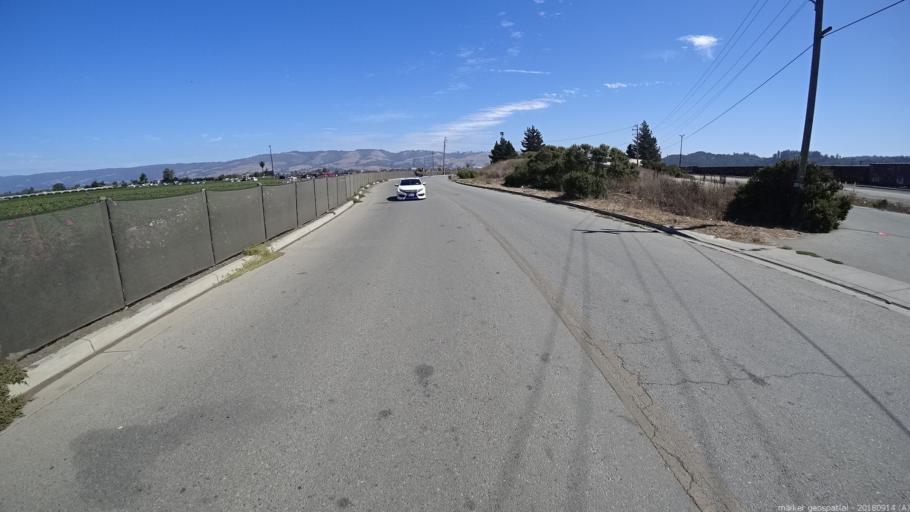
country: US
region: California
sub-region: Monterey County
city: Pajaro
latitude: 36.8974
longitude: -121.7389
